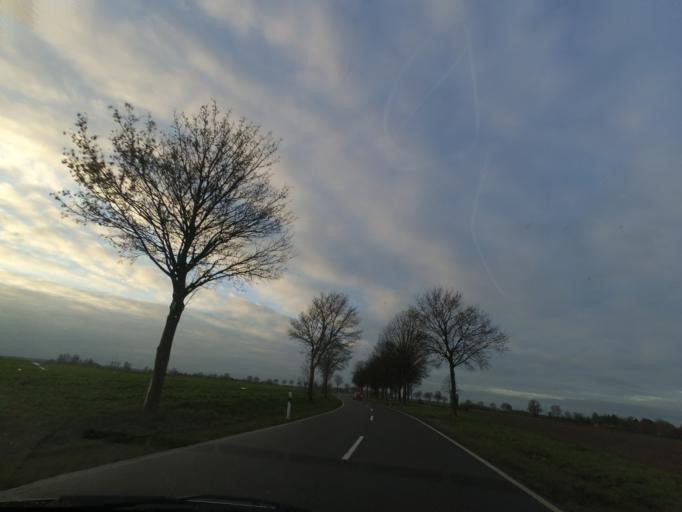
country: DE
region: North Rhine-Westphalia
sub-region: Regierungsbezirk Dusseldorf
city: Juchen
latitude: 51.1330
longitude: 6.5296
